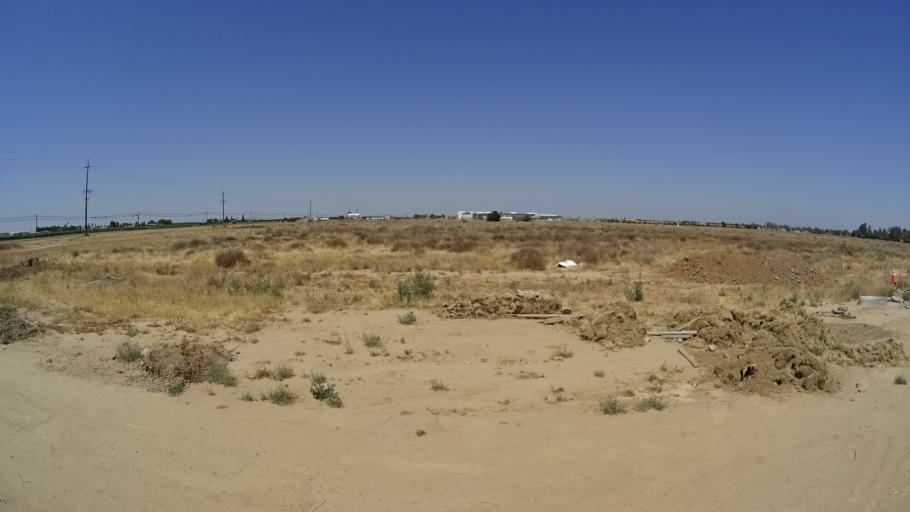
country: US
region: California
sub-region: Fresno County
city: Sunnyside
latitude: 36.7085
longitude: -119.6729
